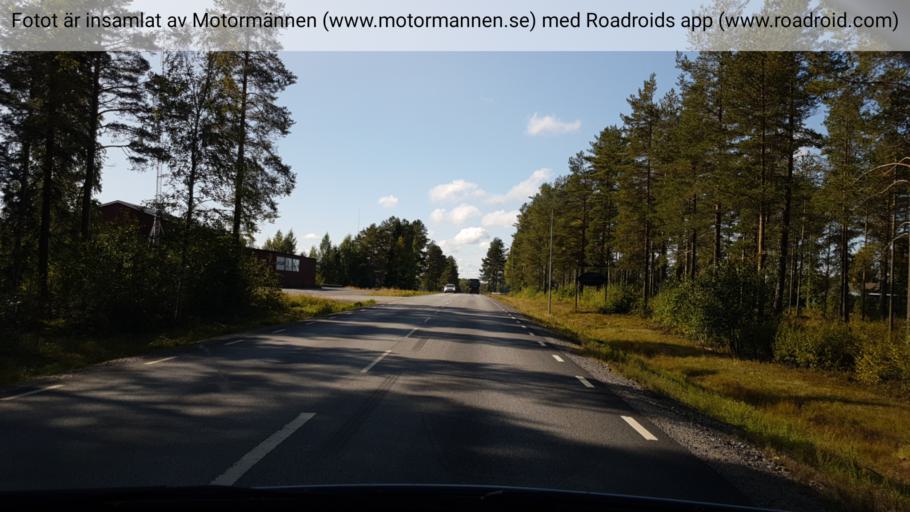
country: SE
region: Vaesterbotten
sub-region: Robertsfors Kommun
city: Robertsfors
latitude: 64.1994
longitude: 20.8508
